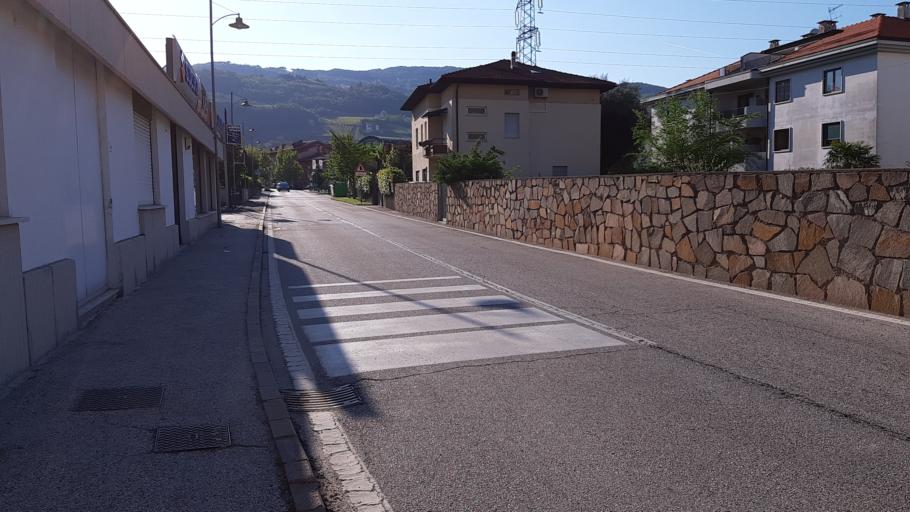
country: IT
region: Trentino-Alto Adige
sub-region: Provincia di Trento
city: Lavis
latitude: 46.1382
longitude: 11.1067
